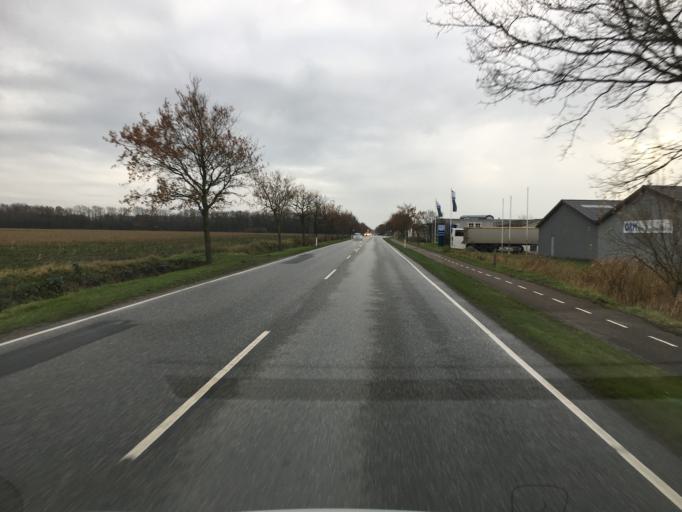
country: DK
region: South Denmark
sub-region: Tonder Kommune
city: Tonder
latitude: 54.9578
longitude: 8.8691
